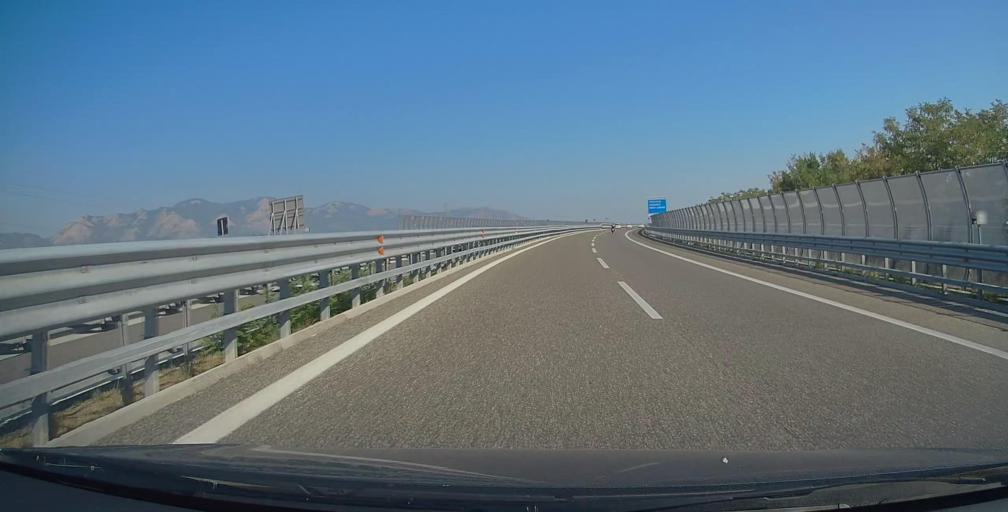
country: IT
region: Campania
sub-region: Provincia di Salerno
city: Sala Consilina
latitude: 40.4106
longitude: 15.5629
